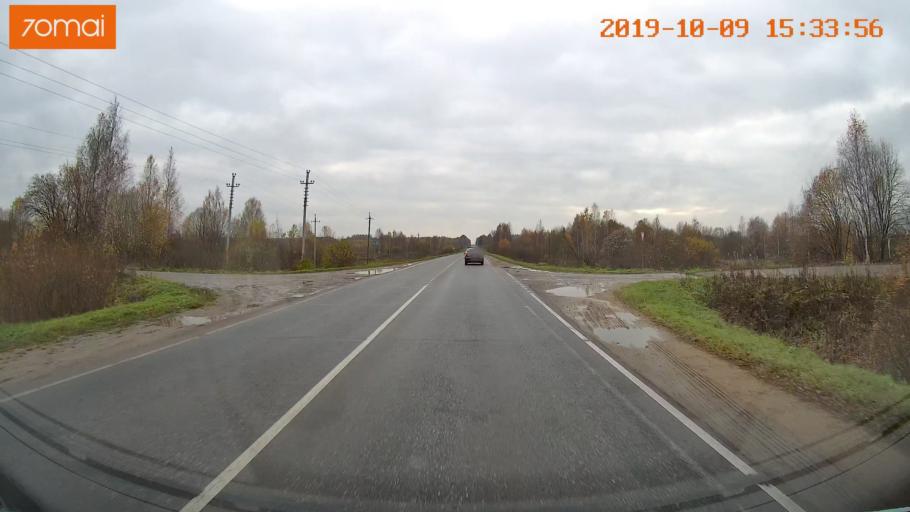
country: RU
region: Kostroma
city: Oktyabr'skiy
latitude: 57.9457
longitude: 41.2546
